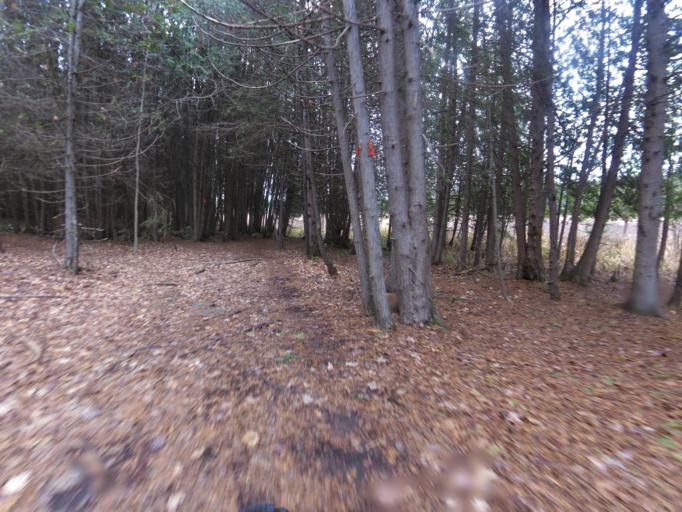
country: CA
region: Ontario
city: Bells Corners
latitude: 45.3097
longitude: -75.8434
